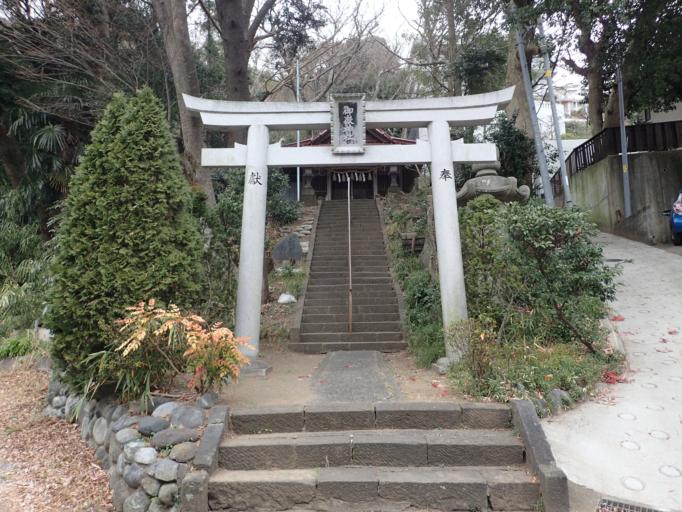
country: JP
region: Kanagawa
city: Oiso
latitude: 35.3112
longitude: 139.3100
